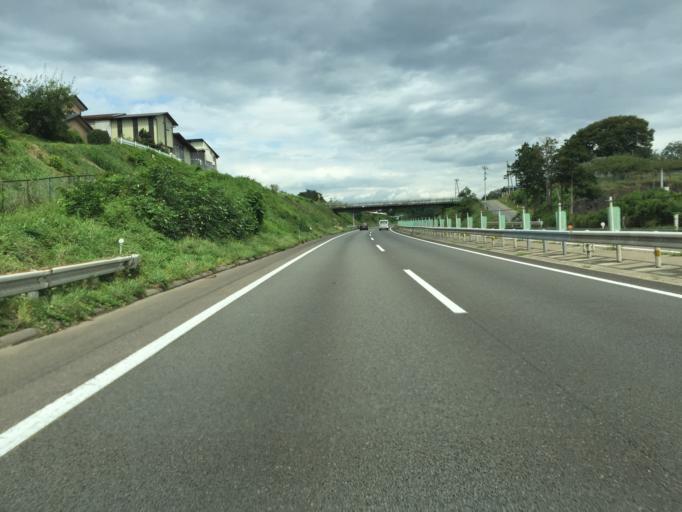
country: JP
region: Miyagi
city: Shiroishi
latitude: 38.0617
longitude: 140.6535
